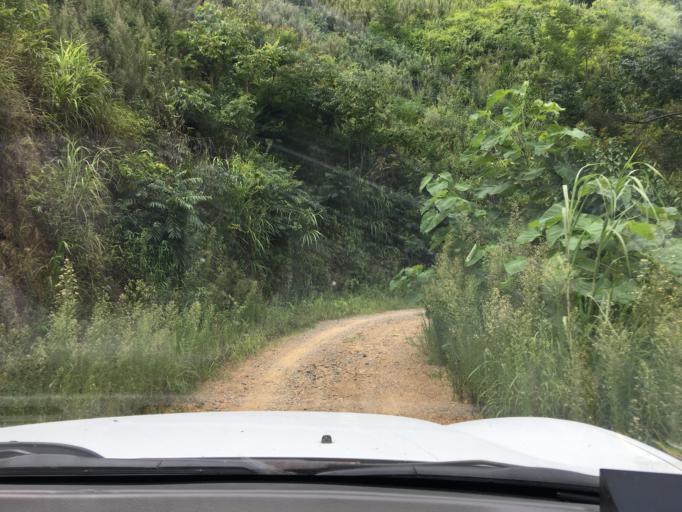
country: CN
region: Guangxi Zhuangzu Zizhiqu
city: Tongle
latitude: 24.9709
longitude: 105.9811
